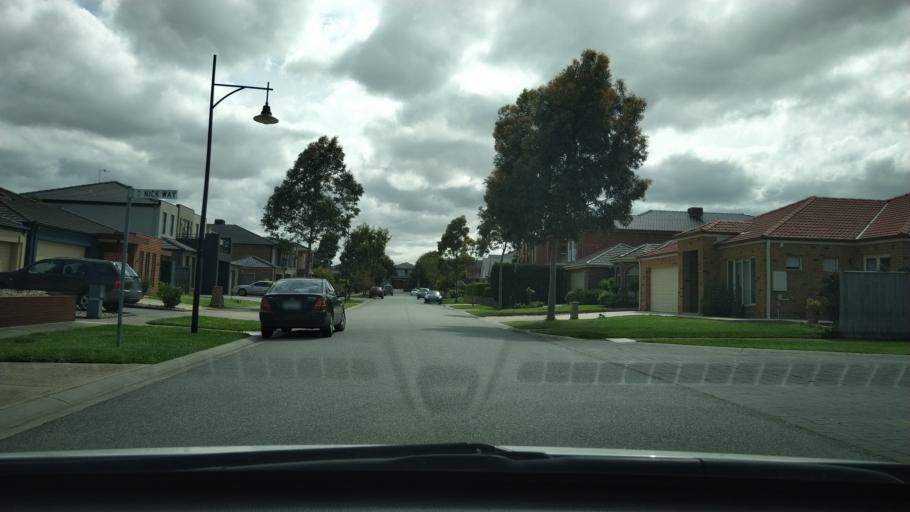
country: AU
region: Victoria
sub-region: Kingston
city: Dingley Village
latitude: -37.9976
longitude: 145.1500
